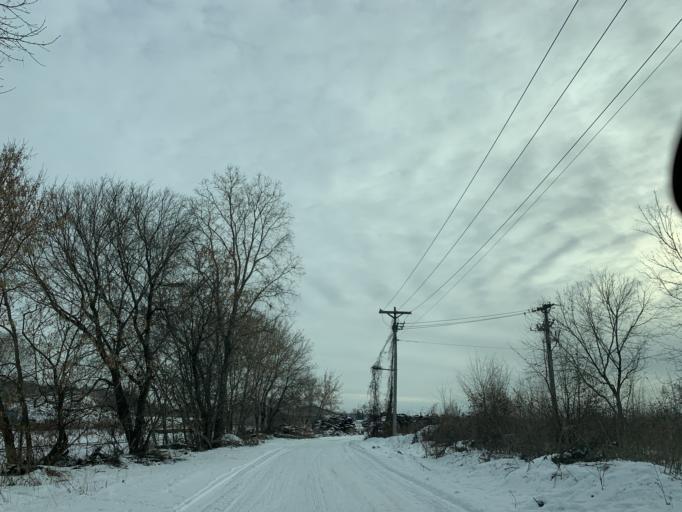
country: US
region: Minnesota
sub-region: Ramsey County
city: Saint Paul
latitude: 44.9457
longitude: -93.0737
